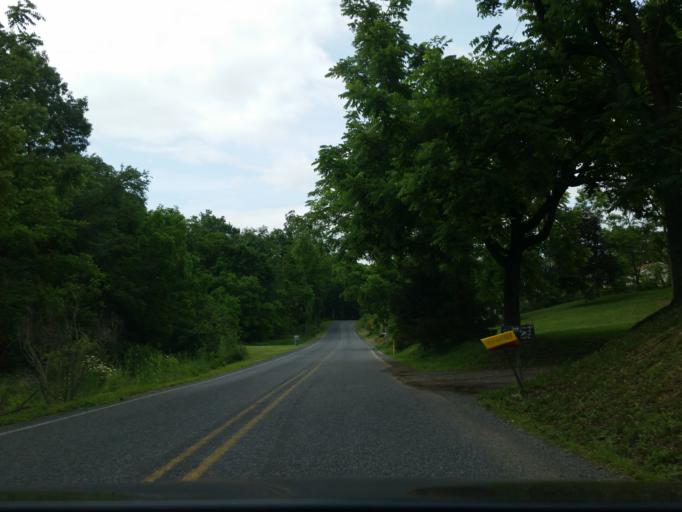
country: US
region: Pennsylvania
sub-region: Lebanon County
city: Jonestown
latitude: 40.4142
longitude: -76.5397
